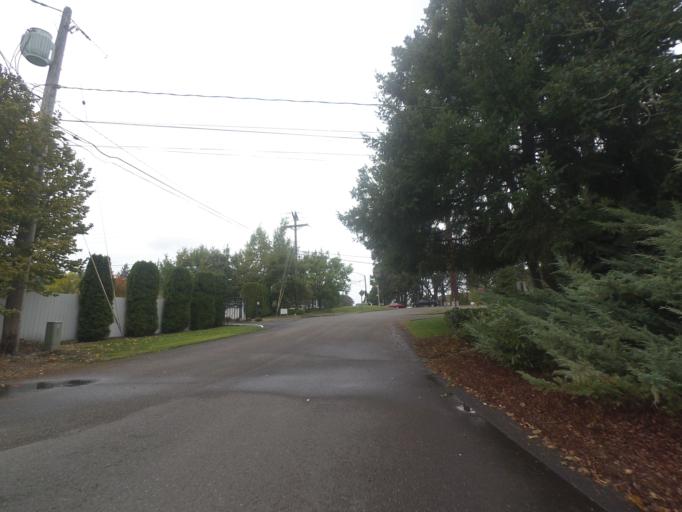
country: US
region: Washington
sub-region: Pierce County
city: Lakewood
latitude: 47.1553
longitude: -122.5205
